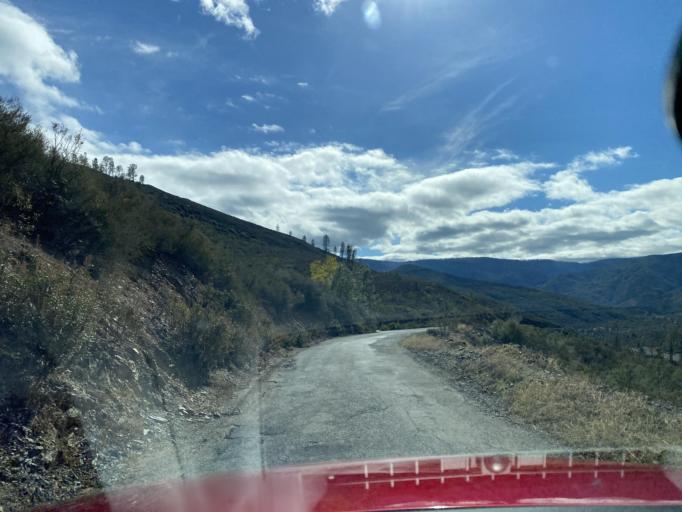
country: US
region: California
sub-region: Lake County
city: Lucerne
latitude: 39.3724
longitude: -122.6523
